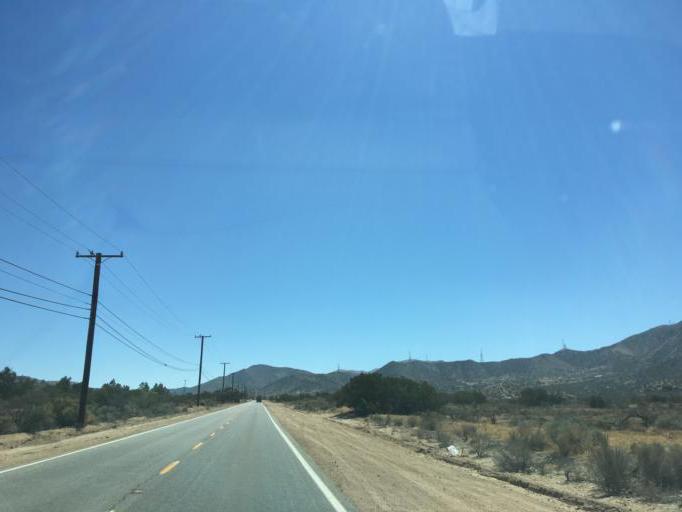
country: US
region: California
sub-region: Los Angeles County
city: Acton
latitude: 34.4809
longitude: -118.1576
